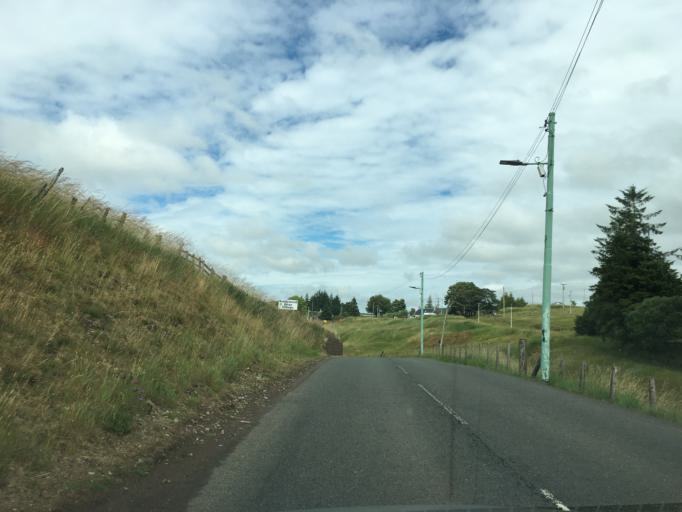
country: GB
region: Scotland
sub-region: Dumfries and Galloway
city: Sanquhar
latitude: 55.4104
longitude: -3.7651
